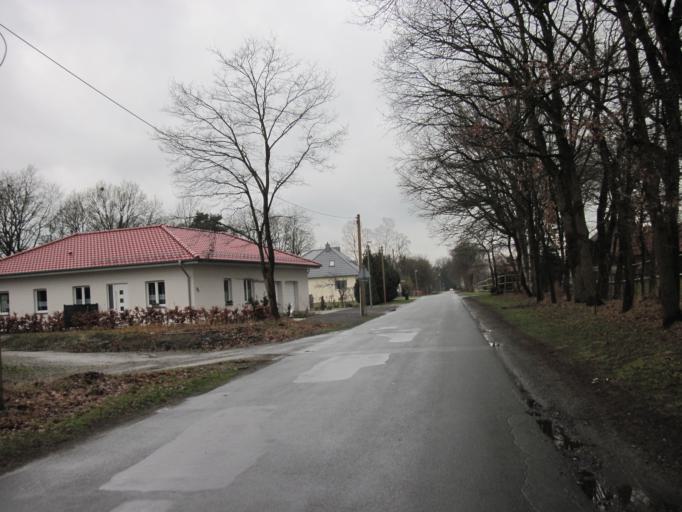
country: DE
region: North Rhine-Westphalia
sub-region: Regierungsbezirk Detmold
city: Hovelhof
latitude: 51.8288
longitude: 8.7044
